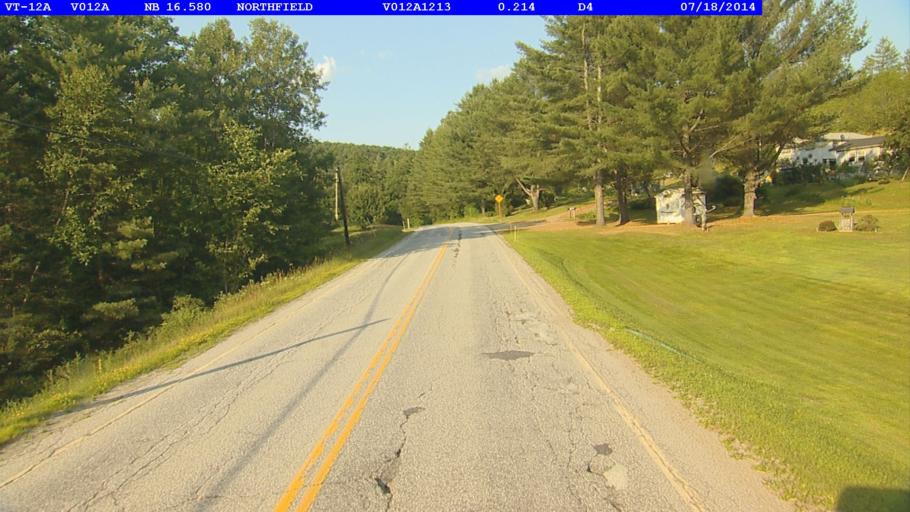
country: US
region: Vermont
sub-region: Washington County
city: Northfield
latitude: 44.1158
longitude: -72.7210
